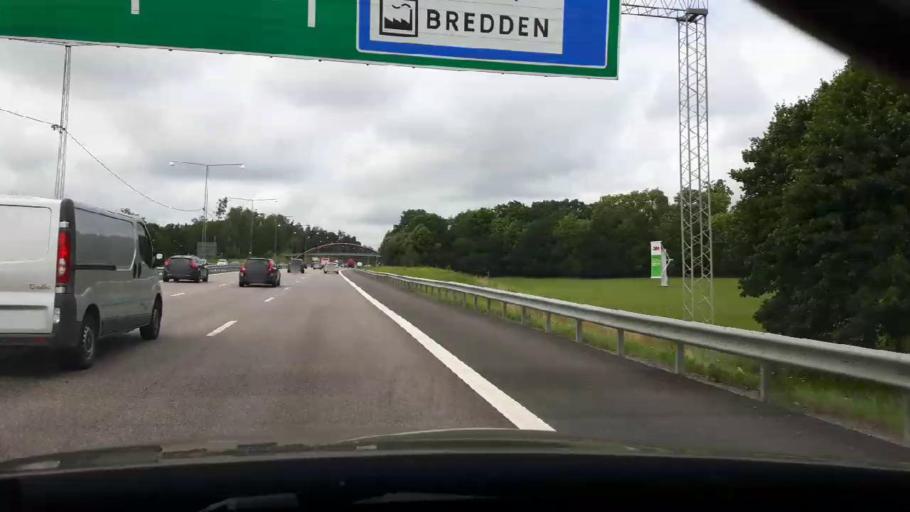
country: SE
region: Stockholm
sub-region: Upplands Vasby Kommun
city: Upplands Vaesby
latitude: 59.4837
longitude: 17.9198
